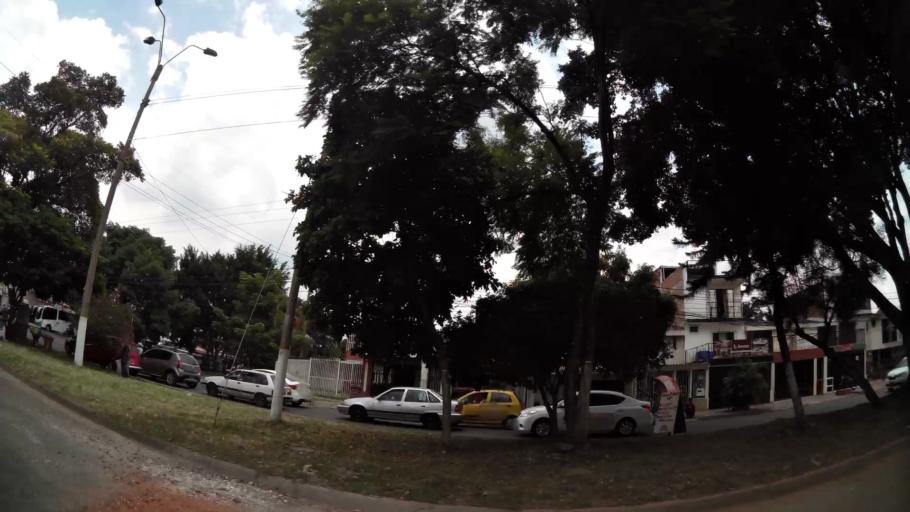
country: CO
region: Valle del Cauca
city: Cali
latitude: 3.4682
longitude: -76.4915
